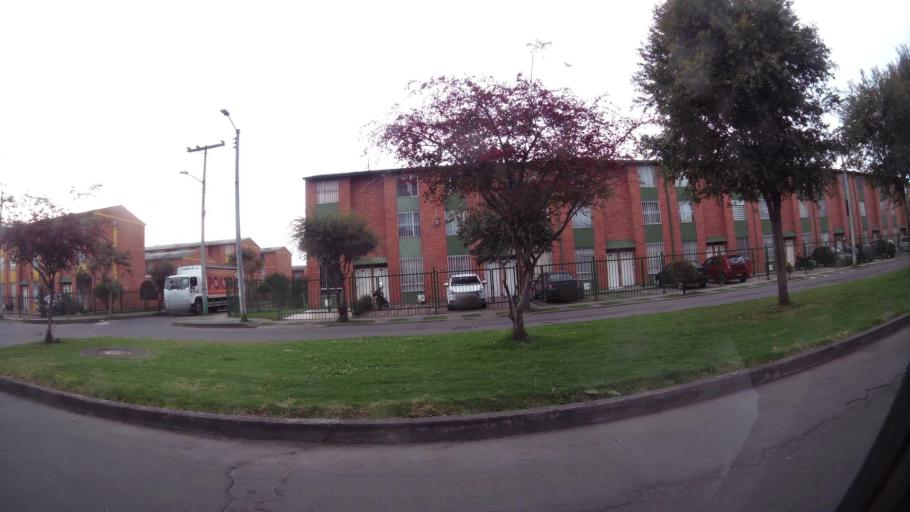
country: CO
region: Cundinamarca
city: Mosquera
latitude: 4.7061
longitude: -74.2236
